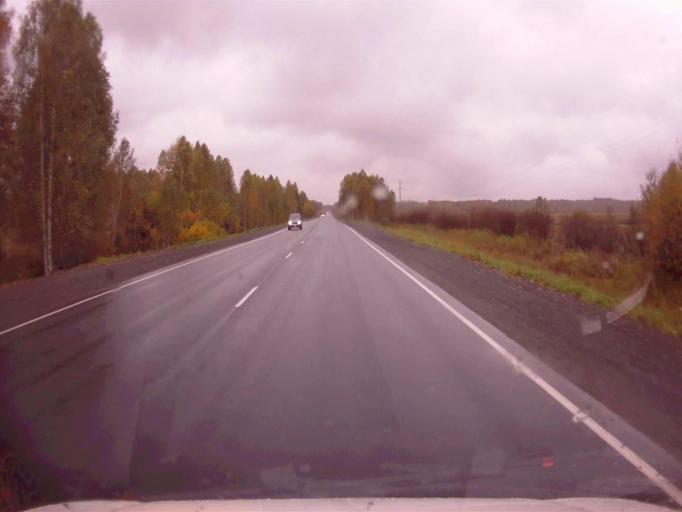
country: RU
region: Chelyabinsk
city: Argayash
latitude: 55.4791
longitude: 60.7997
